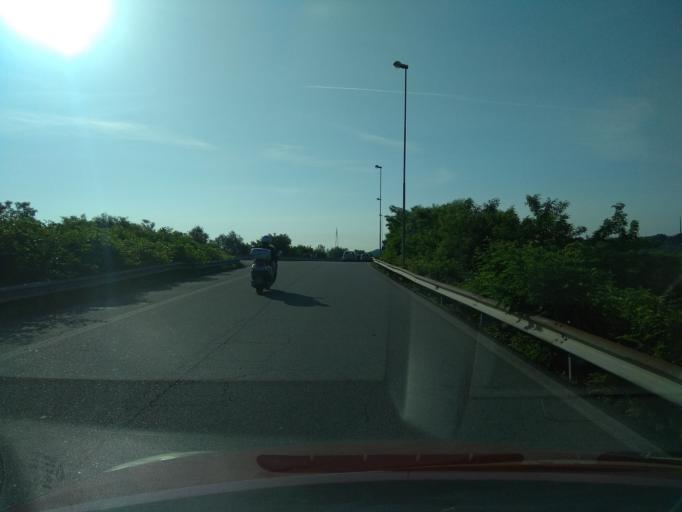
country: IT
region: Piedmont
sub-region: Provincia di Biella
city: Gaglianico
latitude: 45.5597
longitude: 8.0781
